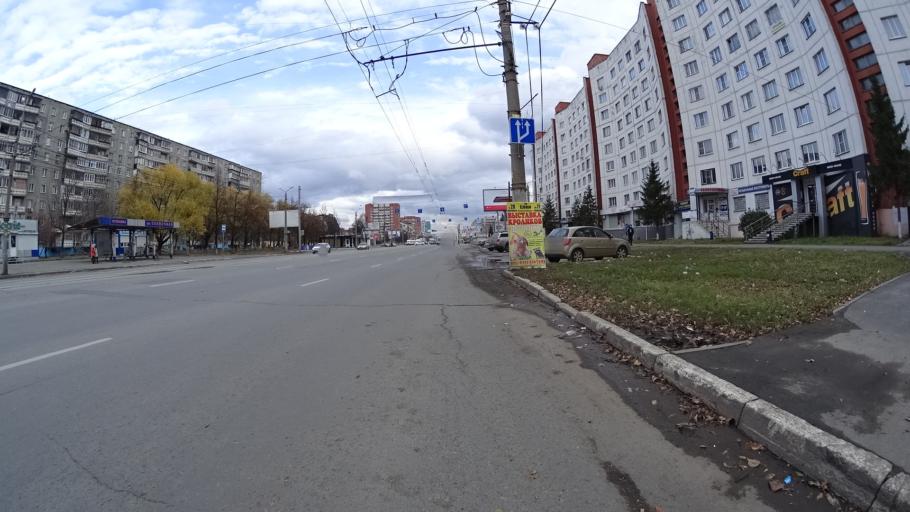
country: RU
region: Chelyabinsk
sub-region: Gorod Chelyabinsk
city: Chelyabinsk
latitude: 55.1943
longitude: 61.3152
